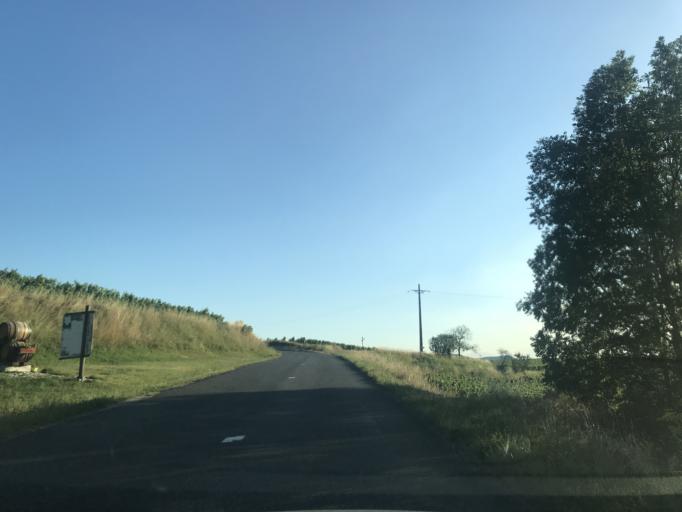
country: FR
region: Rhone-Alpes
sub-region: Departement de la Savoie
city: Yenne
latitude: 45.7293
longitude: 5.7983
